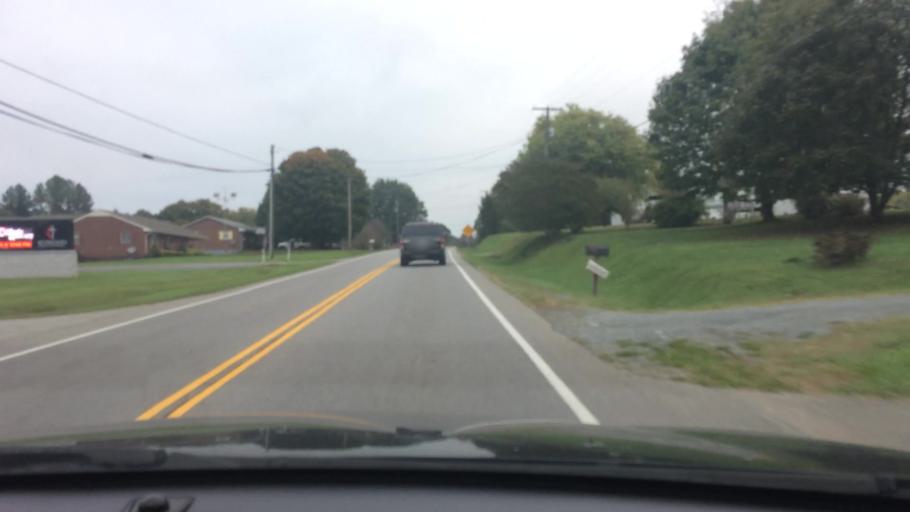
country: US
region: Virginia
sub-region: Franklin County
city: Henry Fork
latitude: 37.0170
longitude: -79.8224
